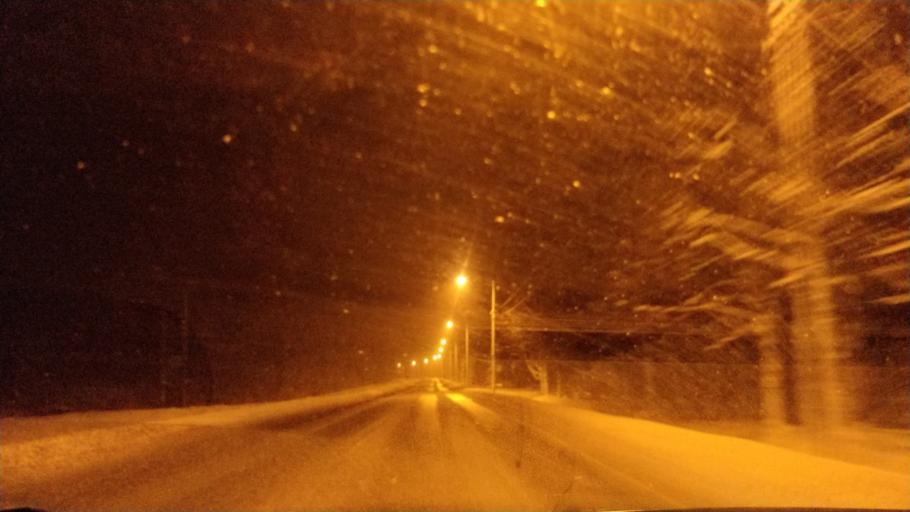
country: FI
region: Lapland
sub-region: Rovaniemi
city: Rovaniemi
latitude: 66.4068
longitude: 25.3966
